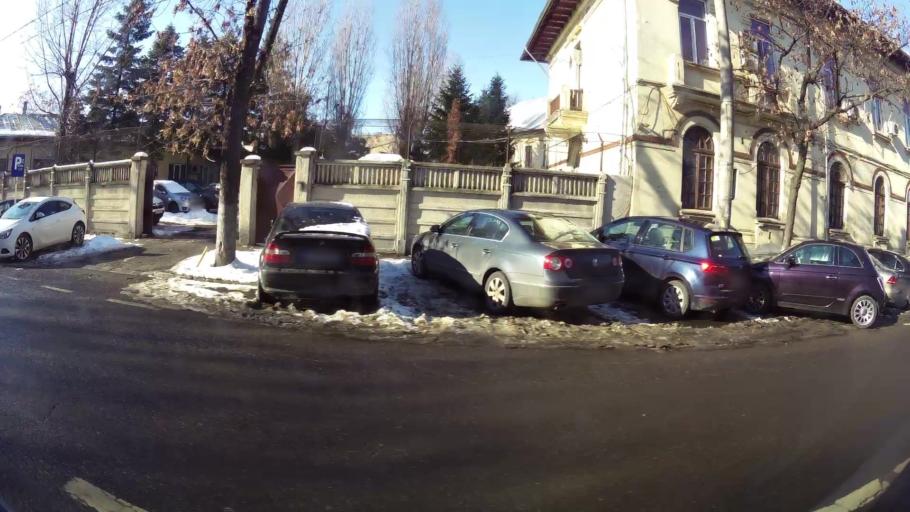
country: RO
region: Bucuresti
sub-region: Municipiul Bucuresti
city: Bucuresti
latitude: 44.4178
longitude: 26.0841
